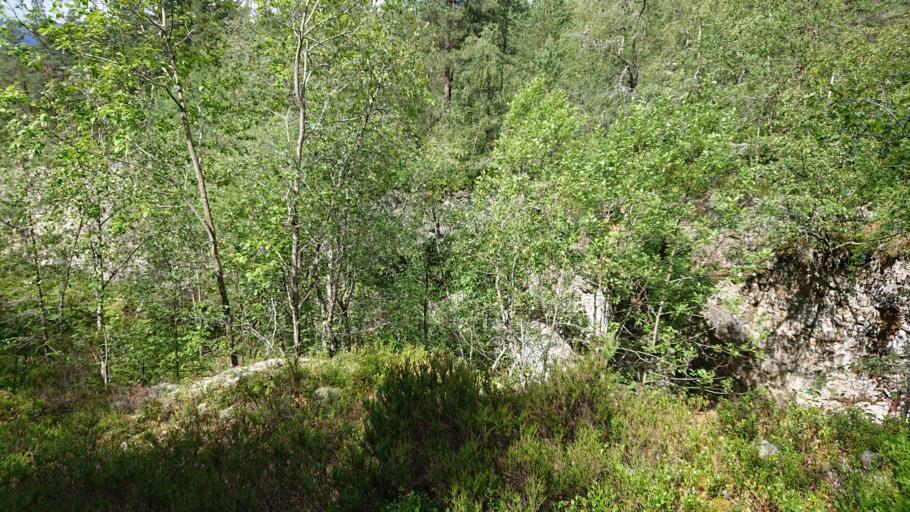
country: NO
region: Aust-Agder
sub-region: Evje og Hornnes
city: Evje
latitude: 58.5974
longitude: 7.8582
